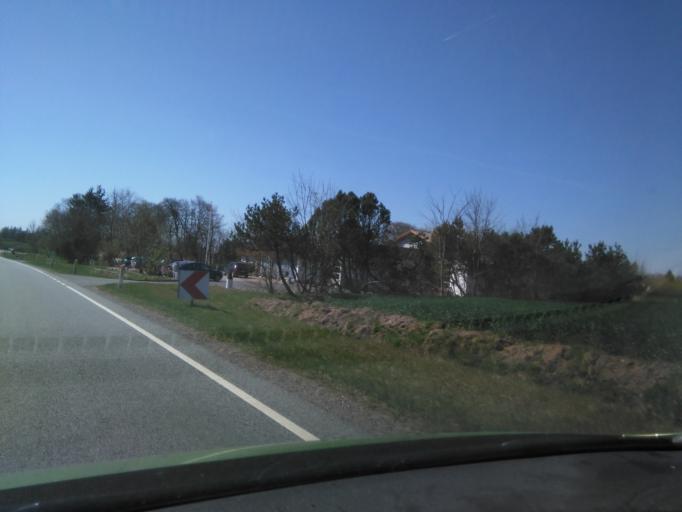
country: DK
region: South Denmark
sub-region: Billund Kommune
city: Grindsted
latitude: 55.6993
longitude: 8.8397
